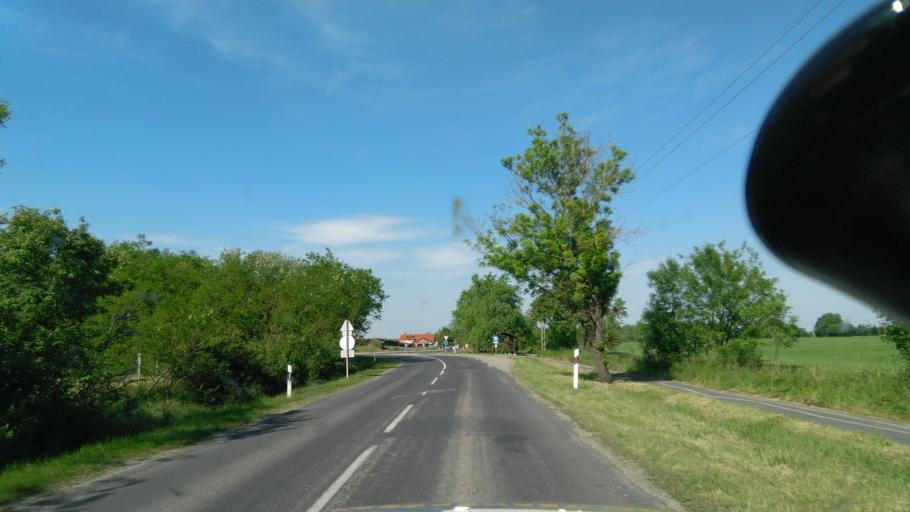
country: HU
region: Bekes
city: Sarkad
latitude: 46.7165
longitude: 21.3310
